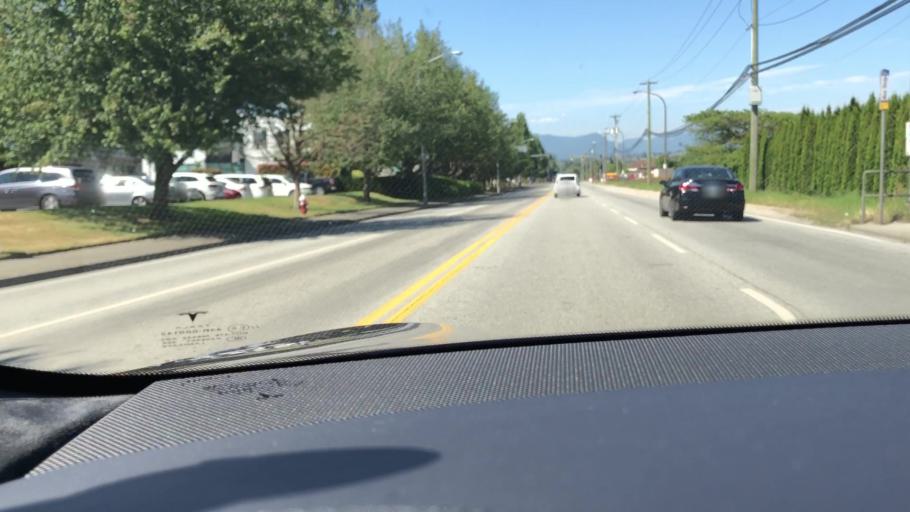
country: CA
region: British Columbia
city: Richmond
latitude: 49.1798
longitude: -123.0692
